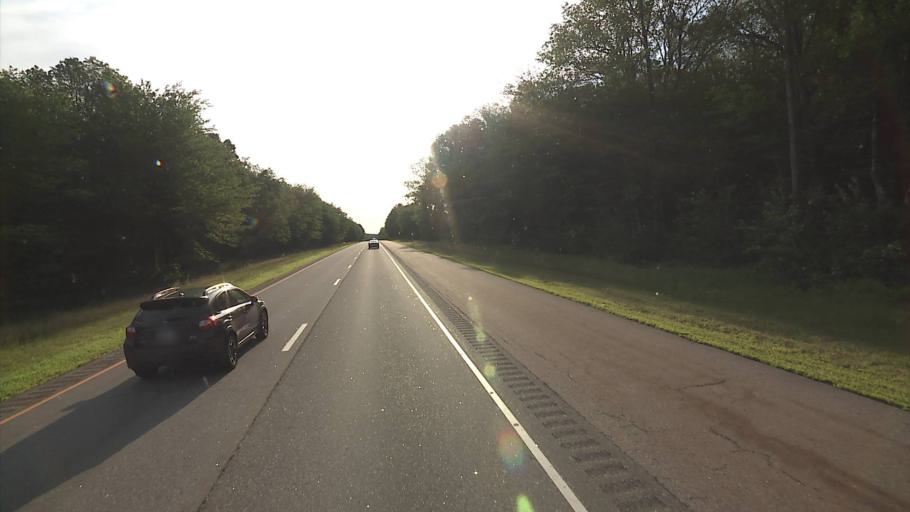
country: US
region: Connecticut
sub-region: New London County
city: Colchester
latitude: 41.5671
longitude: -72.2281
